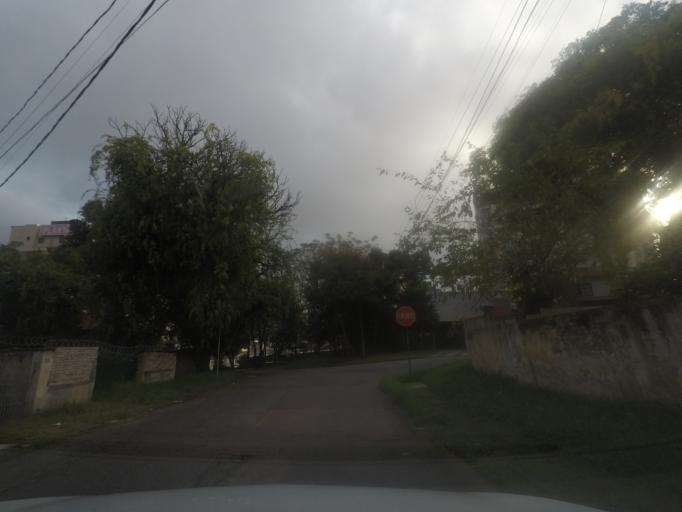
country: BR
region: Parana
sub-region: Curitiba
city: Curitiba
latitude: -25.4326
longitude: -49.2415
